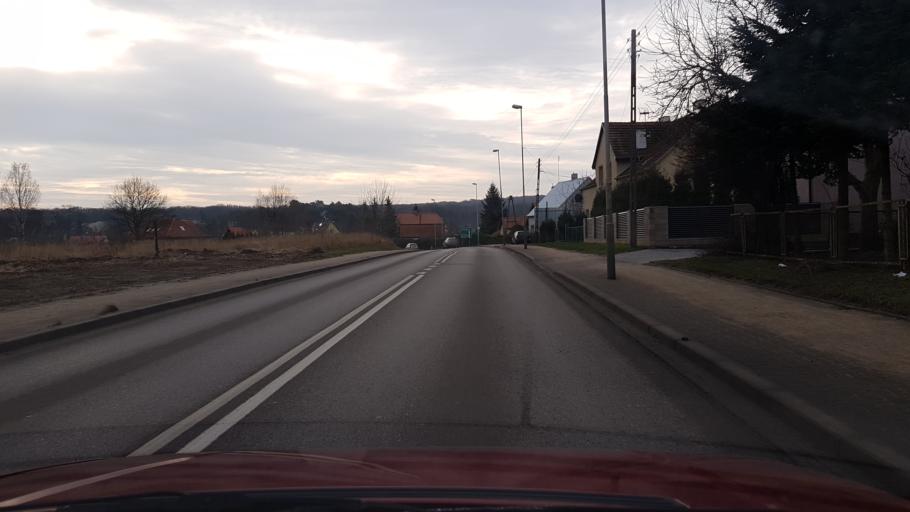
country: PL
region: West Pomeranian Voivodeship
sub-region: Powiat policki
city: Police
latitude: 53.5429
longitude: 14.5750
